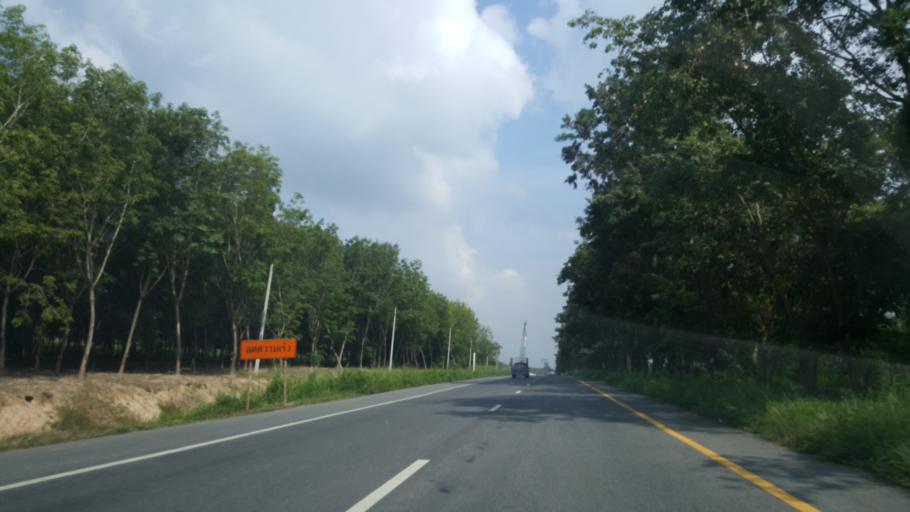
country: TH
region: Rayong
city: Ban Chang
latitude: 12.7743
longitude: 100.9917
